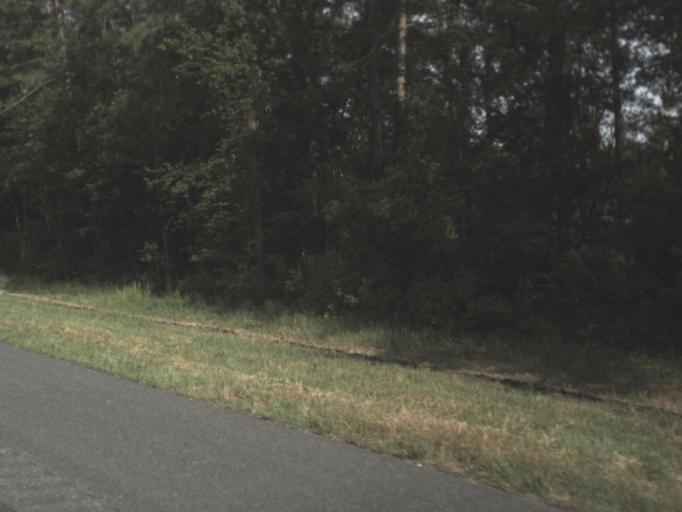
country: US
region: Florida
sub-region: Baker County
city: Macclenny
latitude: 30.2498
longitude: -82.2180
